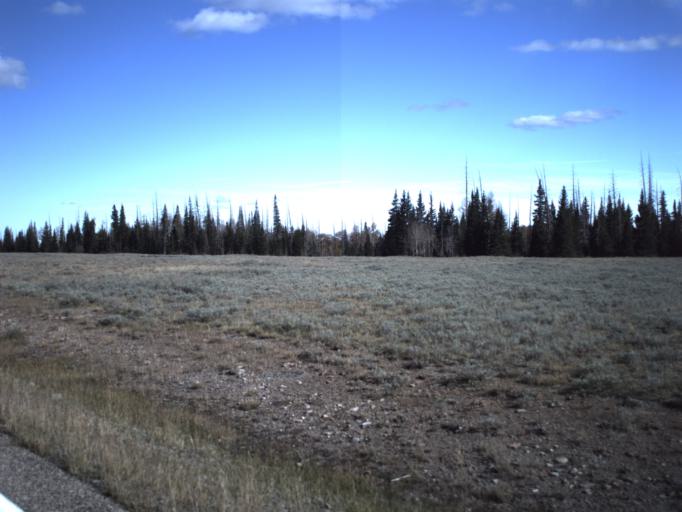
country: US
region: Utah
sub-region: Iron County
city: Parowan
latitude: 37.6541
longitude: -112.7720
